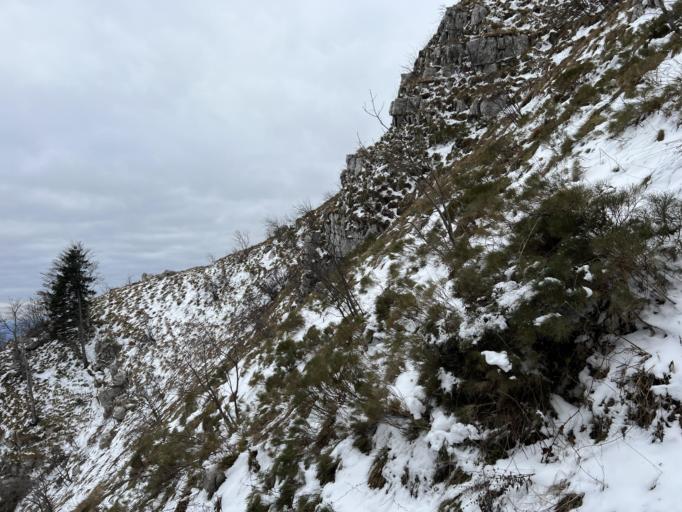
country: IT
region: Friuli Venezia Giulia
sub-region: Provincia di Pordenone
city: Anduins
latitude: 46.2797
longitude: 12.9812
